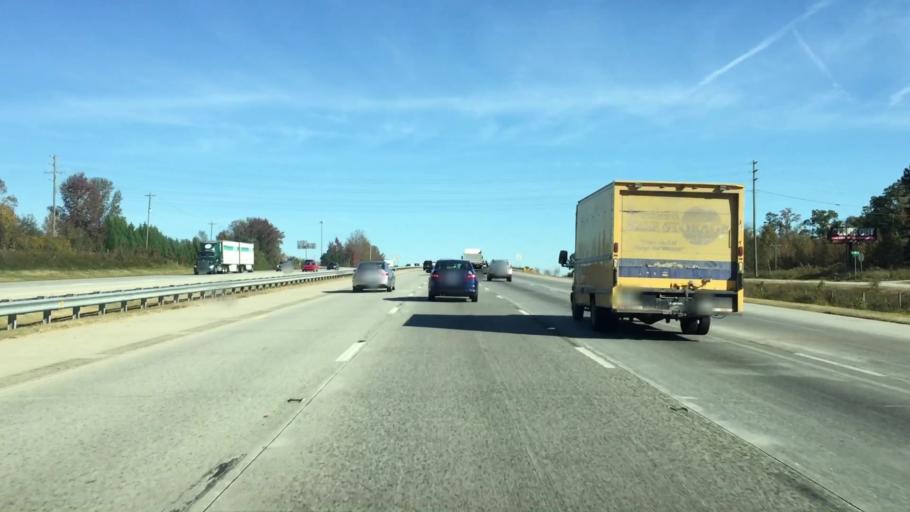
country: US
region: North Carolina
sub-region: Rowan County
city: Spencer
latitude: 35.7051
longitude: -80.3976
